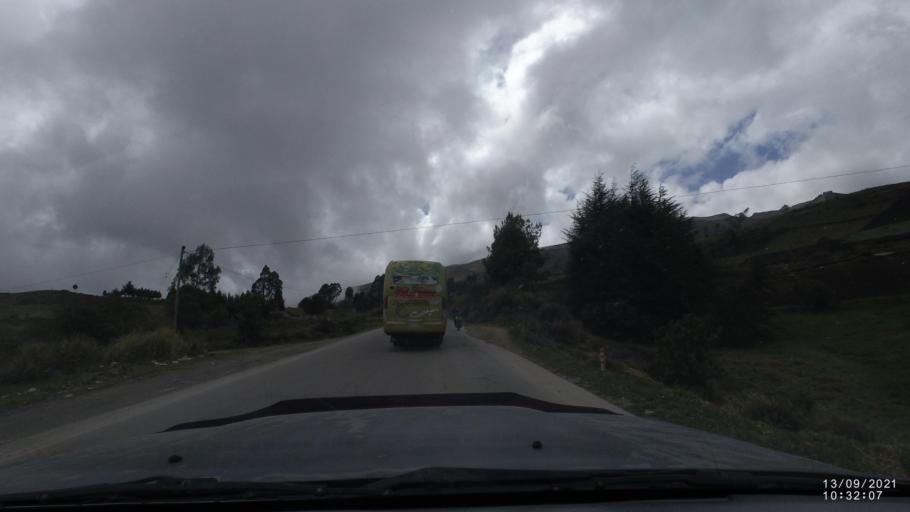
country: BO
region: Cochabamba
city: Colomi
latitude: -17.2501
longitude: -65.8945
